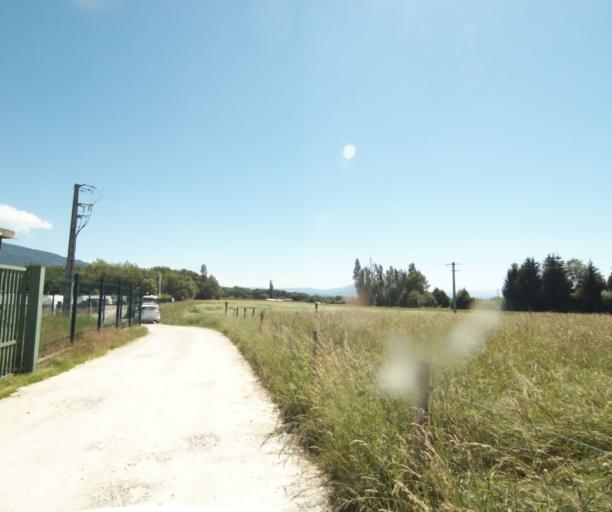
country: FR
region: Rhone-Alpes
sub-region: Departement de la Haute-Savoie
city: Loisin
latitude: 46.2783
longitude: 6.3260
